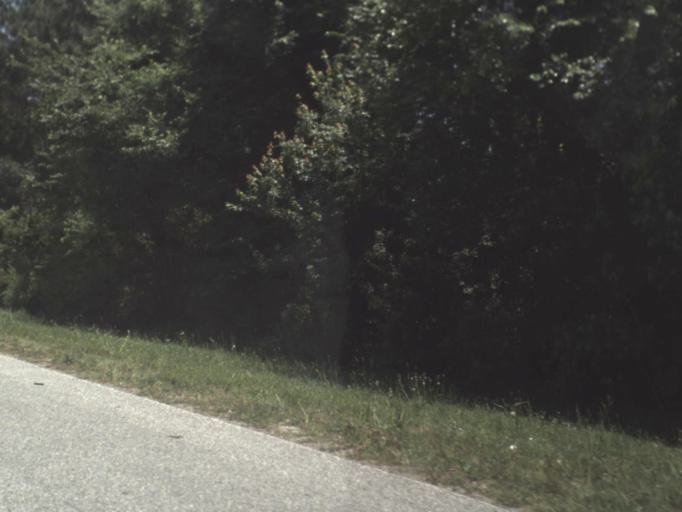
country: US
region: Florida
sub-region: Saint Johns County
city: Fruit Cove
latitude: 30.1719
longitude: -81.6132
